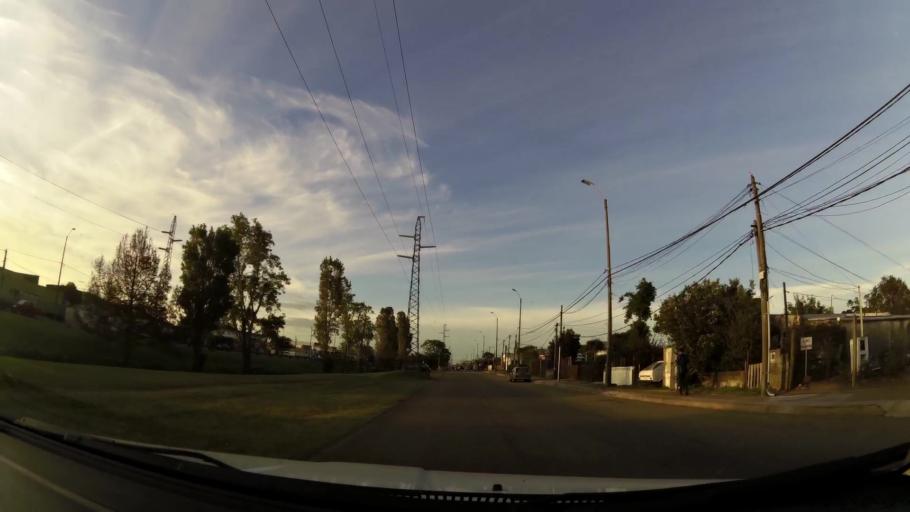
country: UY
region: Maldonado
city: Maldonado
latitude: -34.9125
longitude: -54.9453
